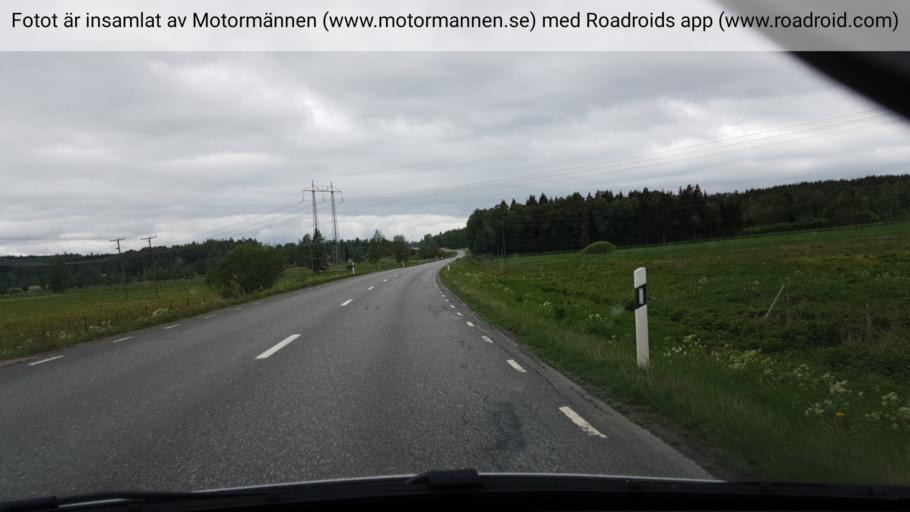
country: SE
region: Joenkoeping
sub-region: Aneby Kommun
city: Aneby
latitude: 57.9816
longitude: 14.8272
